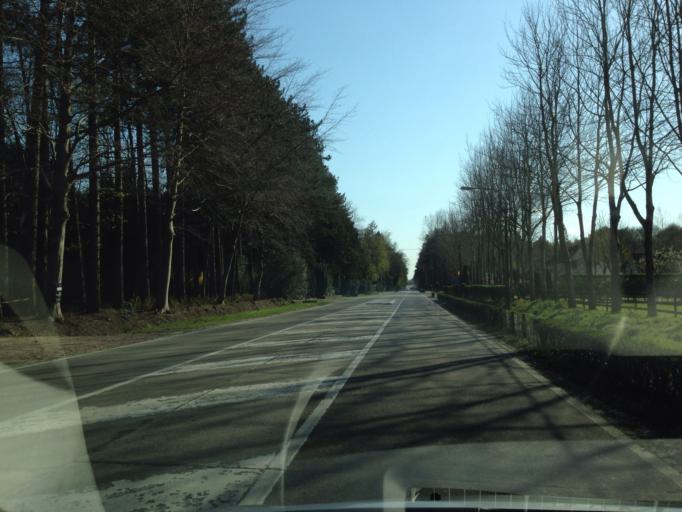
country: BE
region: Flanders
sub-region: Provincie West-Vlaanderen
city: Brugge
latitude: 51.1766
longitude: 3.1817
